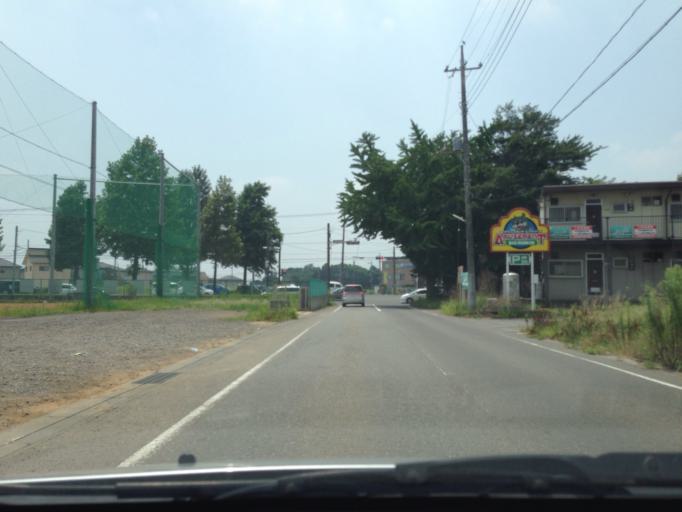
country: JP
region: Ibaraki
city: Naka
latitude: 36.0447
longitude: 140.1252
